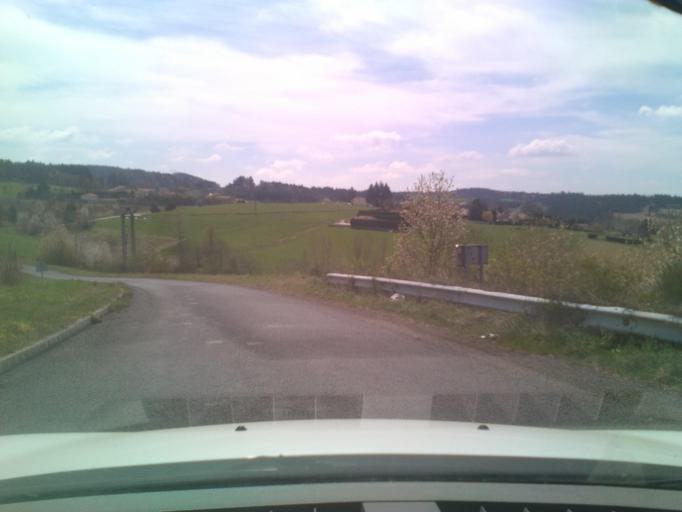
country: FR
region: Auvergne
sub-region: Departement de la Haute-Loire
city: La Seauve-sur-Semene
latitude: 45.3147
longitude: 4.2279
